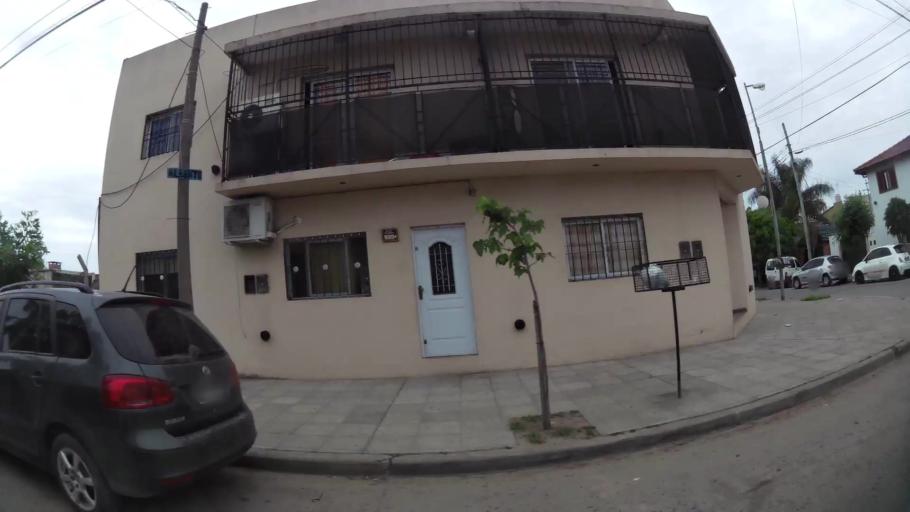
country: AR
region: Buenos Aires
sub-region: Partido de Zarate
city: Zarate
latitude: -34.1100
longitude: -59.0254
